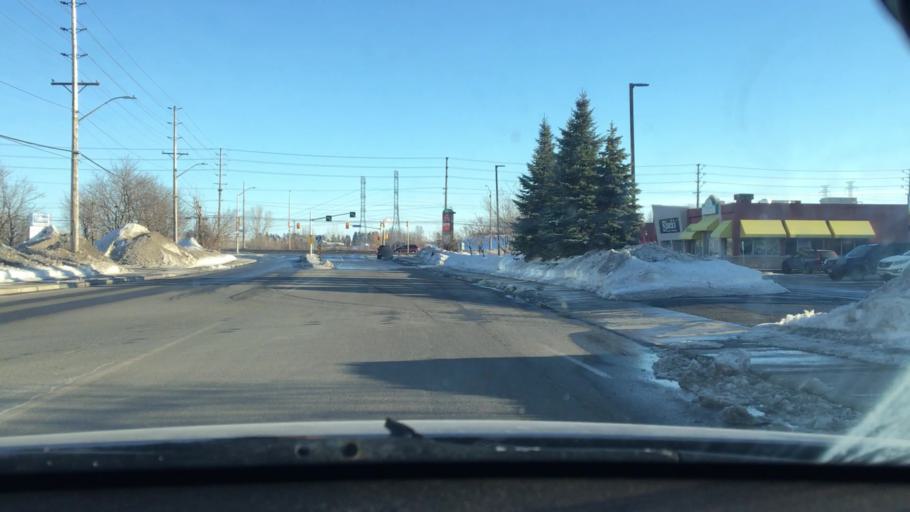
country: CA
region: Ontario
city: Ottawa
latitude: 45.3952
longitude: -75.6054
